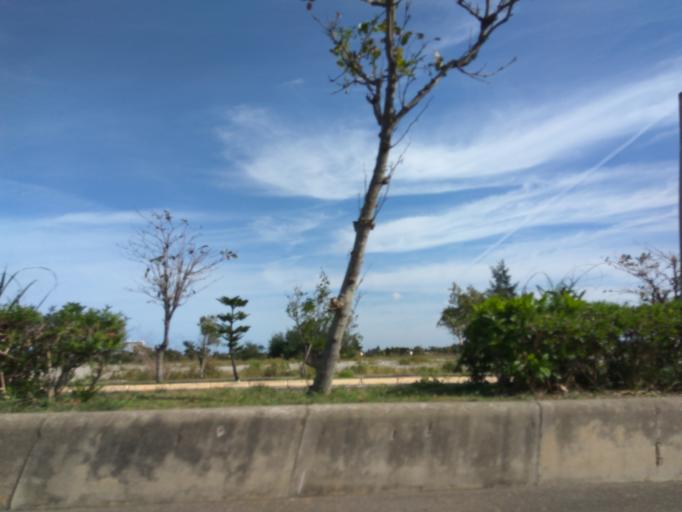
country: TW
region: Taiwan
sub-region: Hsinchu
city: Zhubei
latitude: 25.0344
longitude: 121.0688
